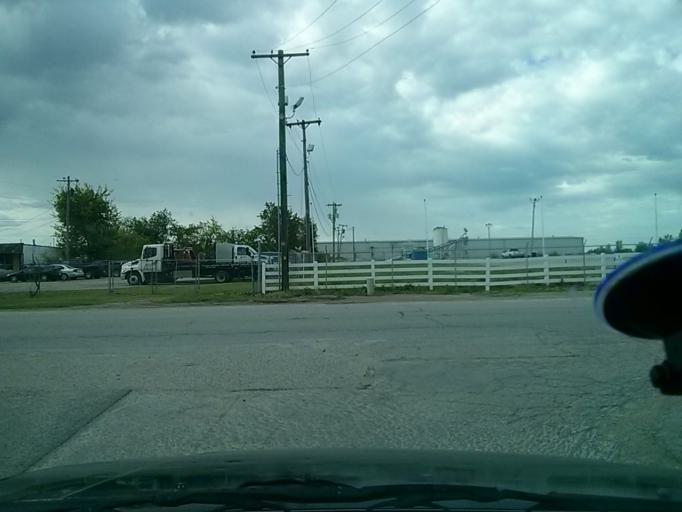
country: US
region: Oklahoma
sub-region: Rogers County
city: Catoosa
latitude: 36.1608
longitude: -95.8389
